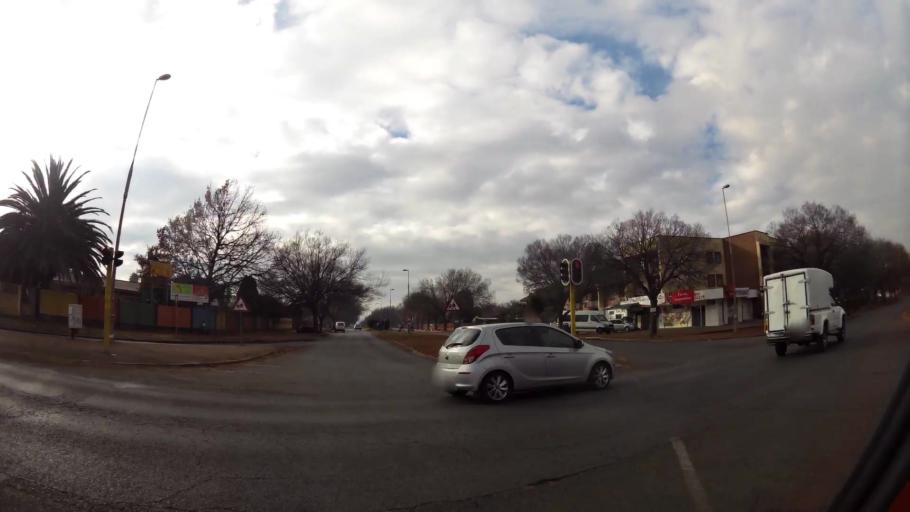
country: ZA
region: Gauteng
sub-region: Sedibeng District Municipality
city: Vanderbijlpark
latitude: -26.6977
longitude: 27.8225
